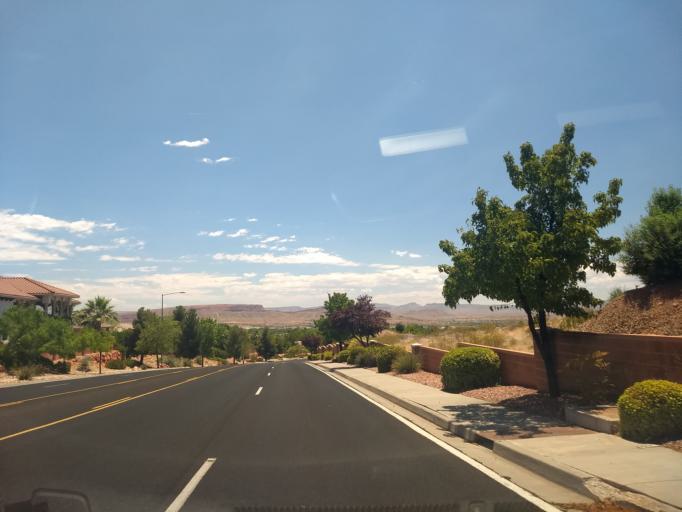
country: US
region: Utah
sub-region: Washington County
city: Washington
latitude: 37.1448
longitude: -113.5301
